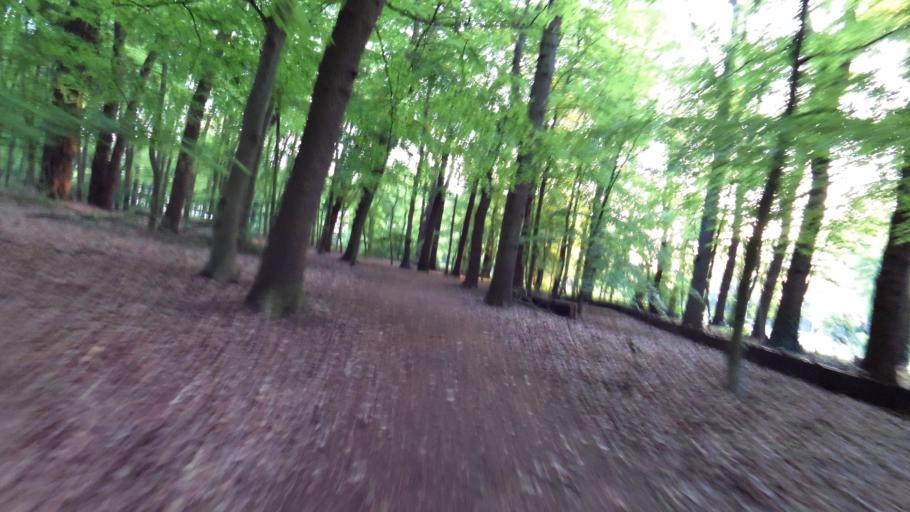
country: NL
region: Gelderland
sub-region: Gemeente Ede
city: Ede
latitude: 52.0191
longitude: 5.6737
